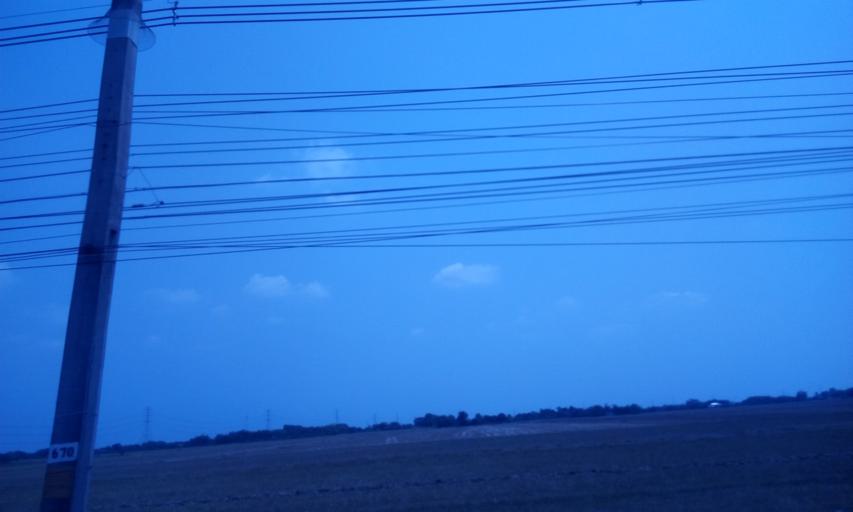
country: TH
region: Chachoengsao
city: Bang Nam Priao
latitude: 13.8186
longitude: 101.0535
